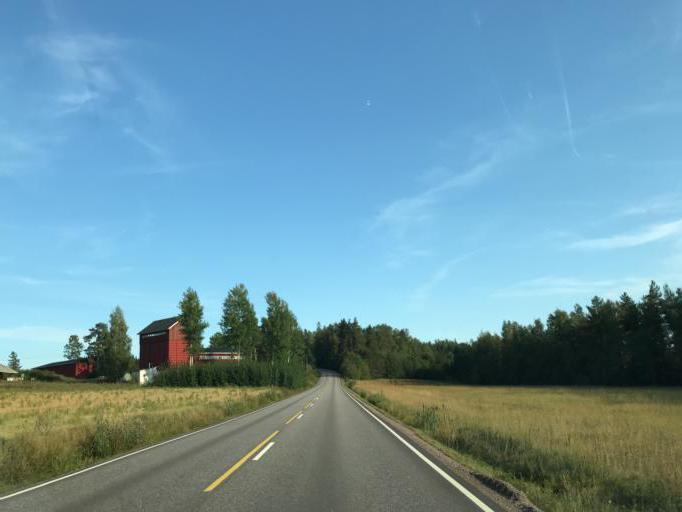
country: FI
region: Uusimaa
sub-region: Helsinki
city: Vihti
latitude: 60.4214
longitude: 24.3665
